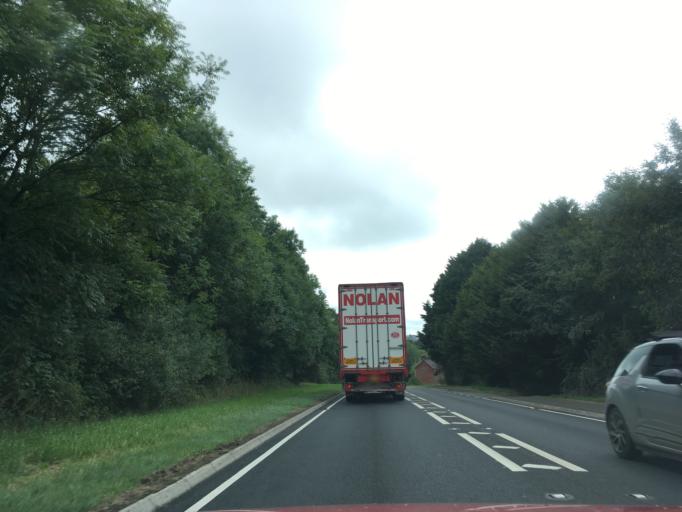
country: GB
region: Wales
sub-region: Pembrokeshire
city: Haverfordwest
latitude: 51.8052
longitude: -4.9471
